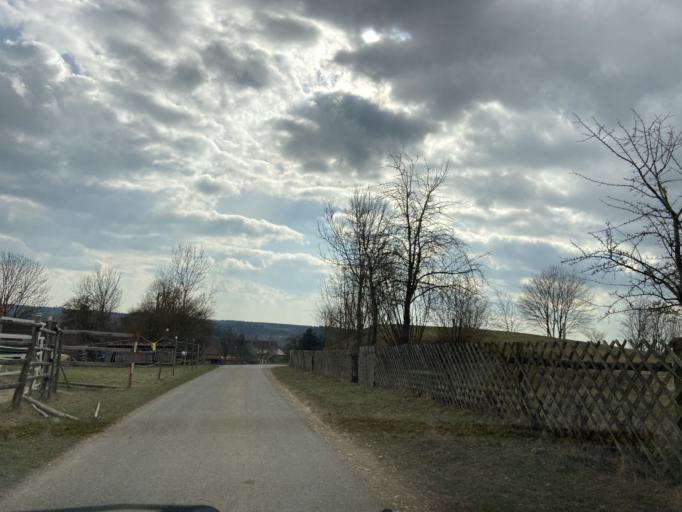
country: DE
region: Baden-Wuerttemberg
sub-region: Tuebingen Region
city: Bingen
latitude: 48.1155
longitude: 9.2594
